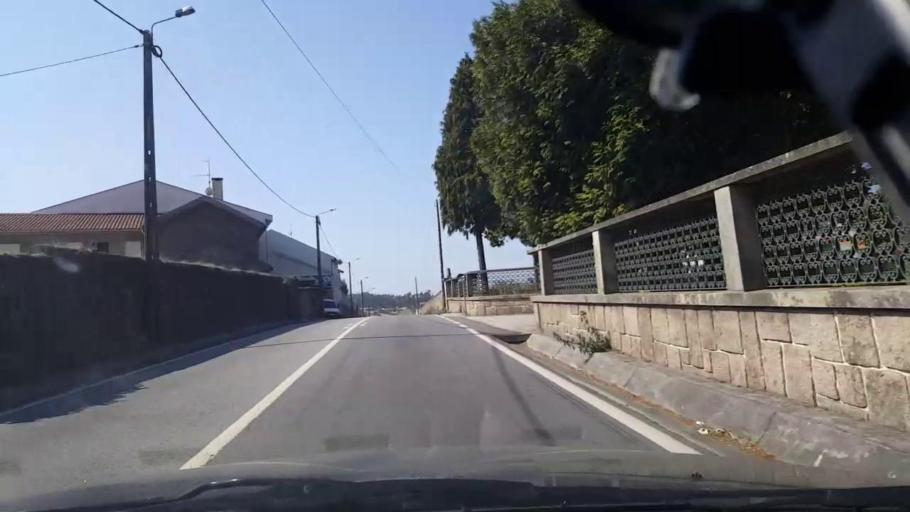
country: PT
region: Porto
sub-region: Povoa de Varzim
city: Pedroso
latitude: 41.3874
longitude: -8.7074
